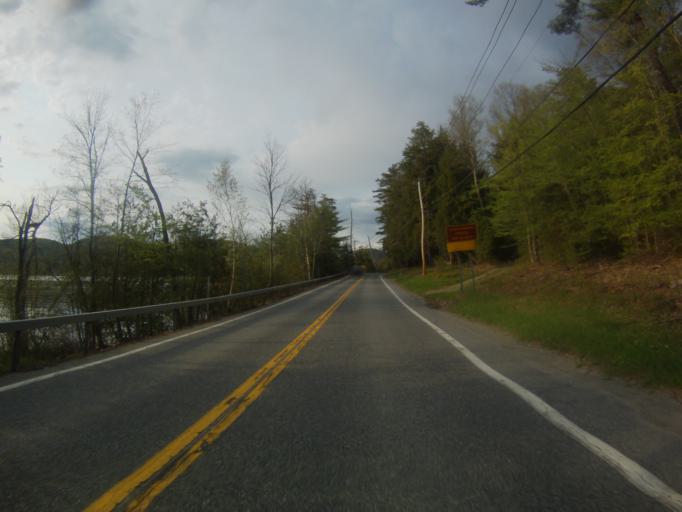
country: US
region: New York
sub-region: Warren County
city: Warrensburg
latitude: 43.7001
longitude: -73.7136
